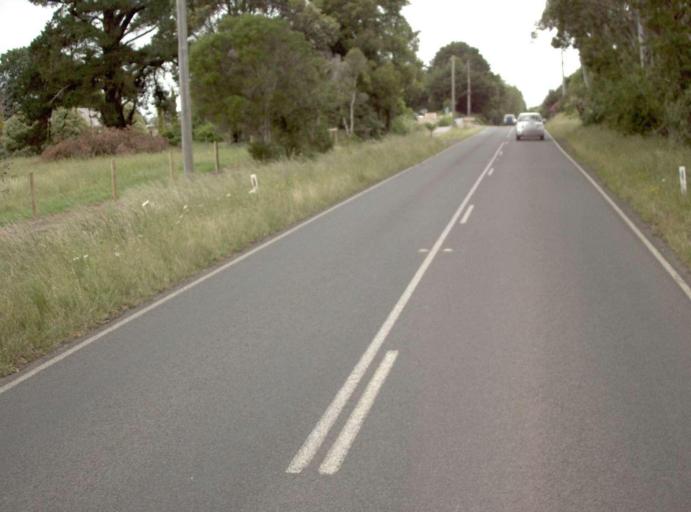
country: AU
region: Victoria
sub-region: Baw Baw
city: Warragul
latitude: -38.1648
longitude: 145.9751
